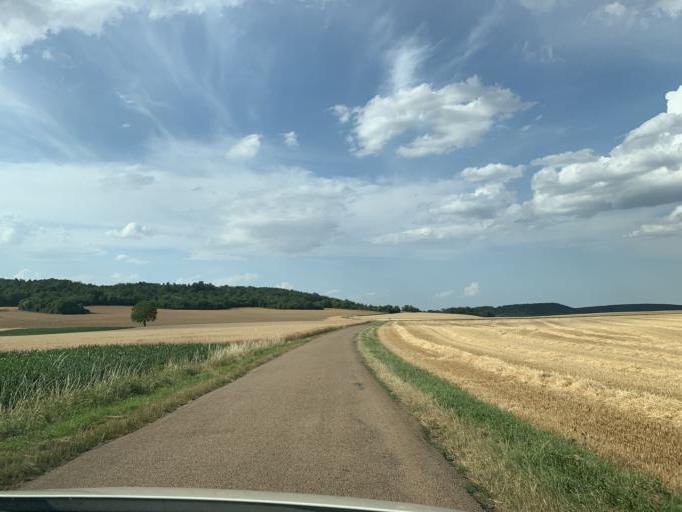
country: FR
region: Bourgogne
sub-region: Departement de la Nievre
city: Clamecy
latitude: 47.4583
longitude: 3.4248
